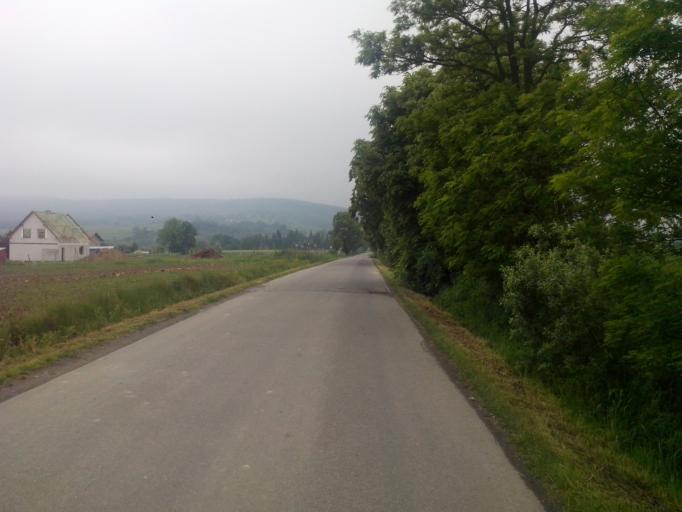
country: PL
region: Subcarpathian Voivodeship
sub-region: Powiat strzyzowski
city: Strzyzow
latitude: 49.8519
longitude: 21.7787
